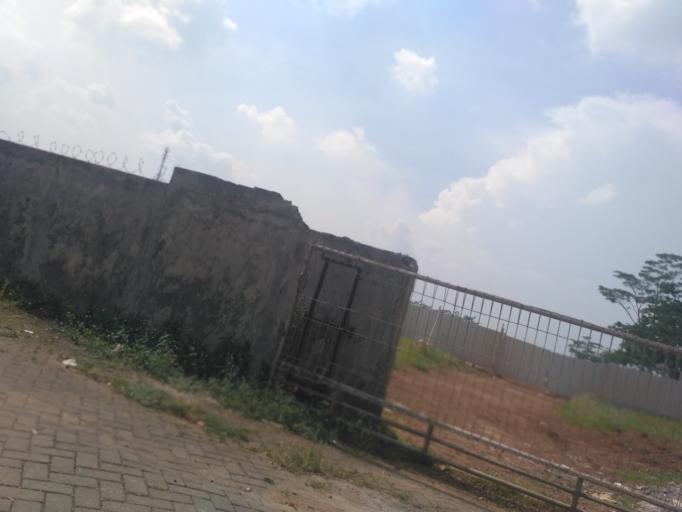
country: ID
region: Central Java
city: Ungaran
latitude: -7.0708
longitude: 110.4432
